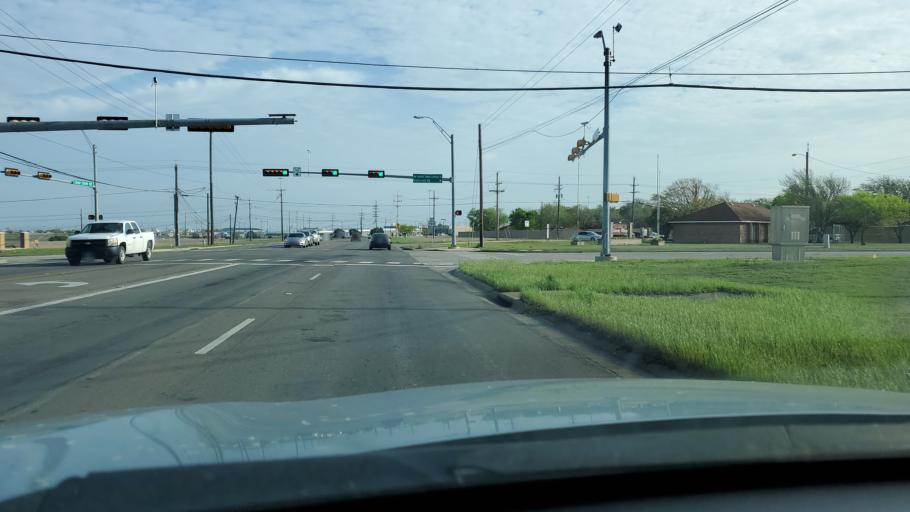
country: US
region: Texas
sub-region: Bell County
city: Fort Hood
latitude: 31.1159
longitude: -97.7985
